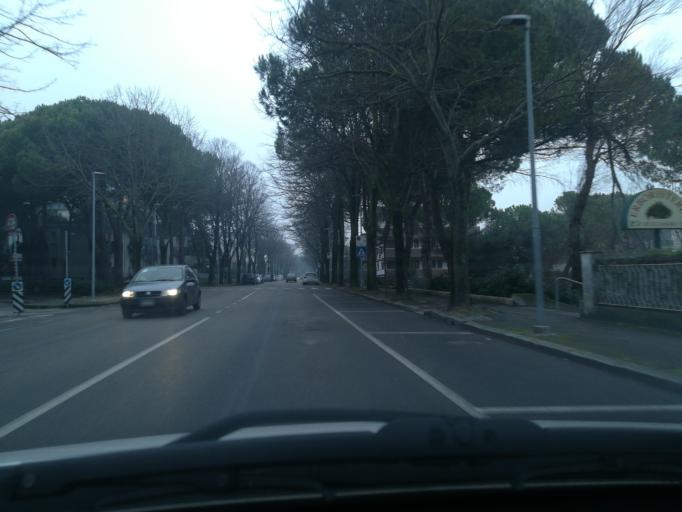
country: IT
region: Emilia-Romagna
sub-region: Provincia di Rimini
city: Riccione
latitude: 44.0068
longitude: 12.6453
